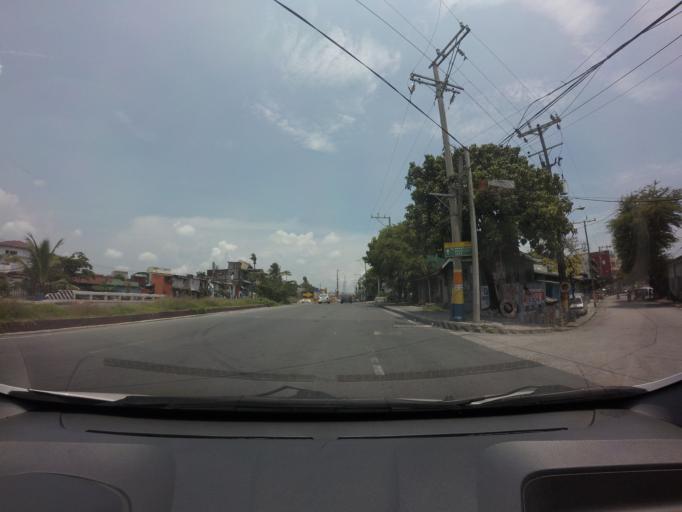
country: PH
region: Metro Manila
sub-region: City of Manila
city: Quiapo
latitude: 14.5908
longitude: 121.0016
